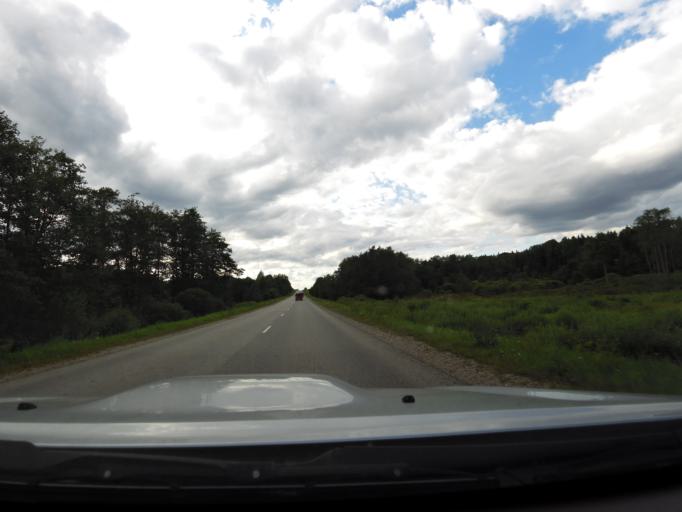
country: LV
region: Ilukste
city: Ilukste
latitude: 55.9687
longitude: 26.0346
